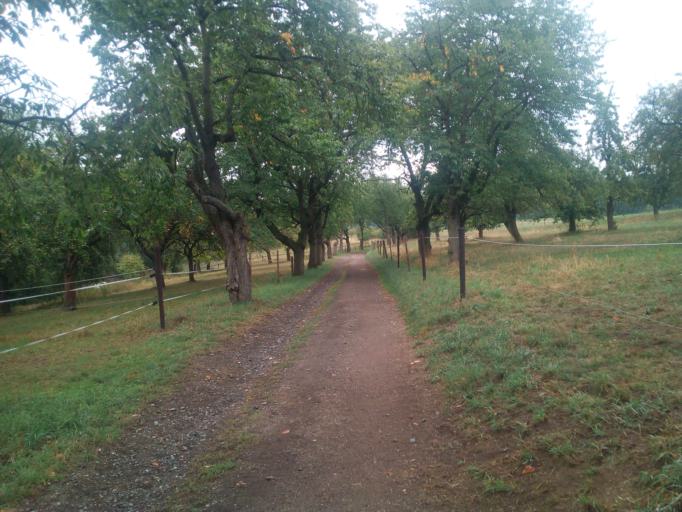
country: DE
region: Saxony
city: Kreischa
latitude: 50.9340
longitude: 13.7817
